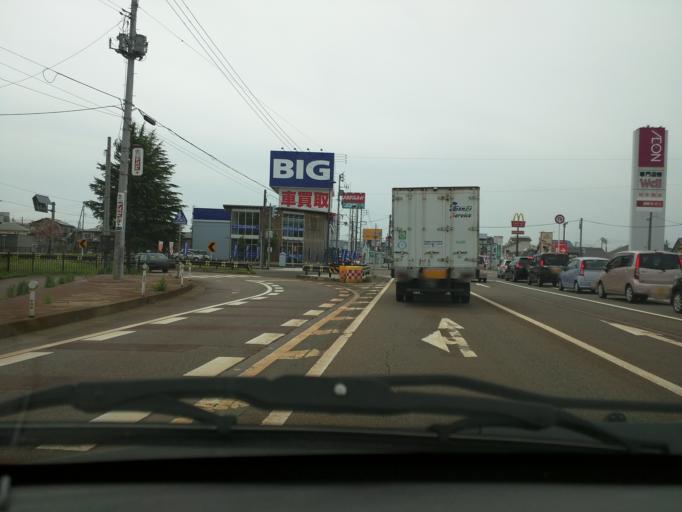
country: JP
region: Niigata
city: Nagaoka
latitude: 37.4526
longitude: 138.8239
